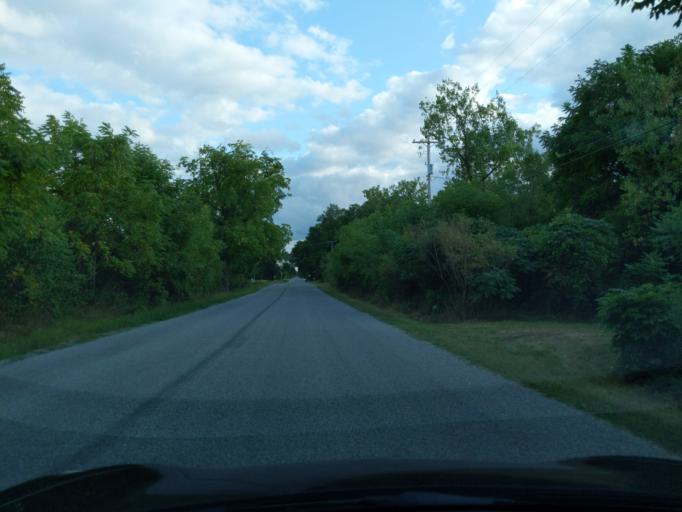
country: US
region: Michigan
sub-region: Eaton County
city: Dimondale
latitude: 42.6344
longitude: -84.5824
